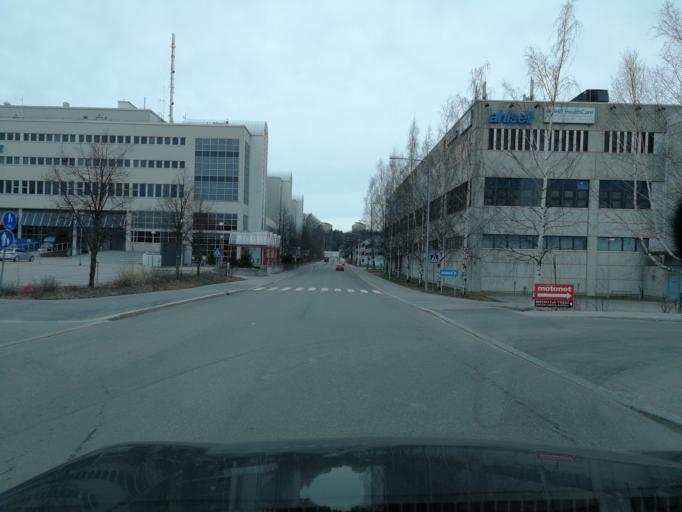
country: FI
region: Uusimaa
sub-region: Helsinki
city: Vantaa
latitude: 60.2092
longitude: 25.0560
